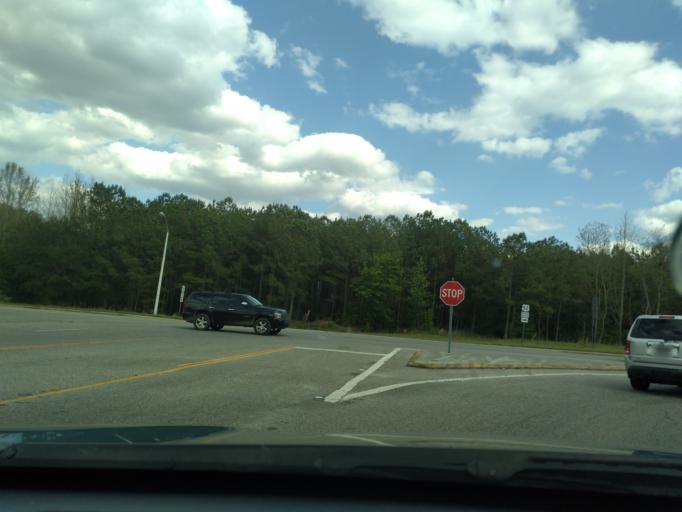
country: US
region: South Carolina
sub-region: Florence County
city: Florence
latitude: 34.1572
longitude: -79.7581
